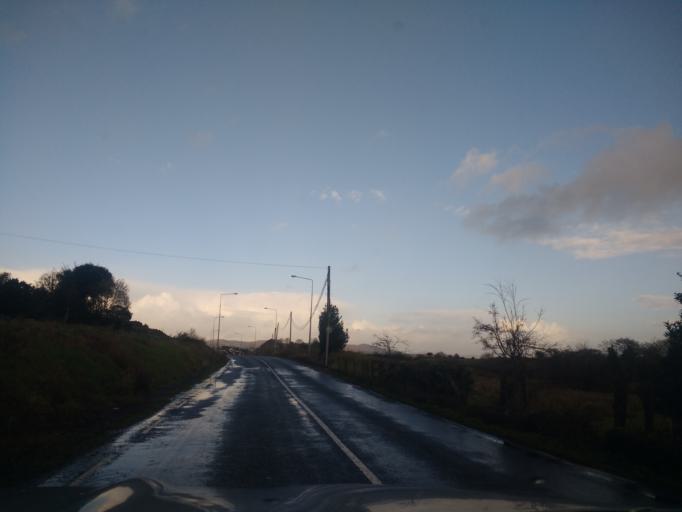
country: IE
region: Ulster
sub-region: County Donegal
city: Ramelton
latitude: 55.0259
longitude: -7.6501
